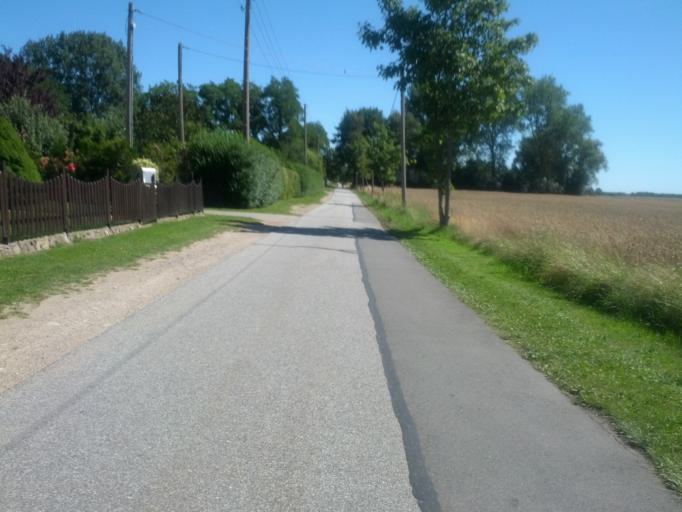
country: DE
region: Mecklenburg-Vorpommern
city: Bastorf
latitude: 54.1219
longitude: 11.6513
